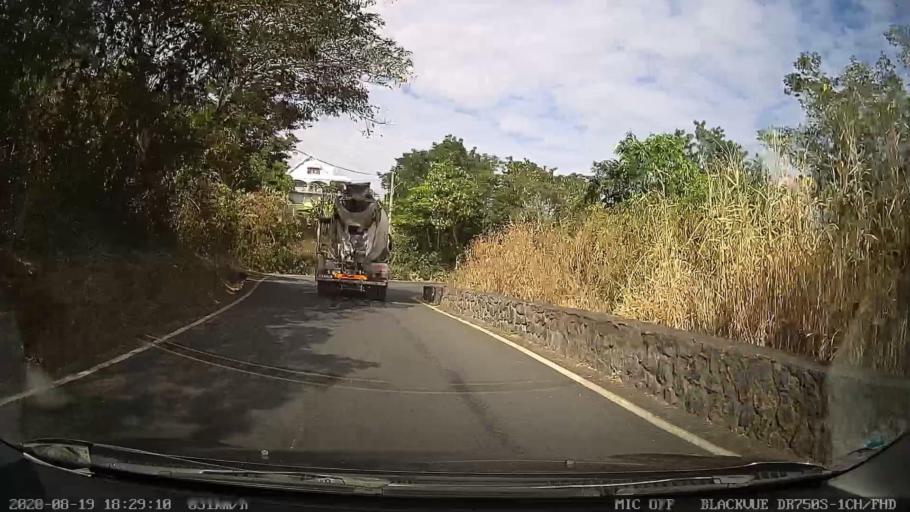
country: RE
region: Reunion
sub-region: Reunion
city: La Possession
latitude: -20.9574
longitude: 55.3497
